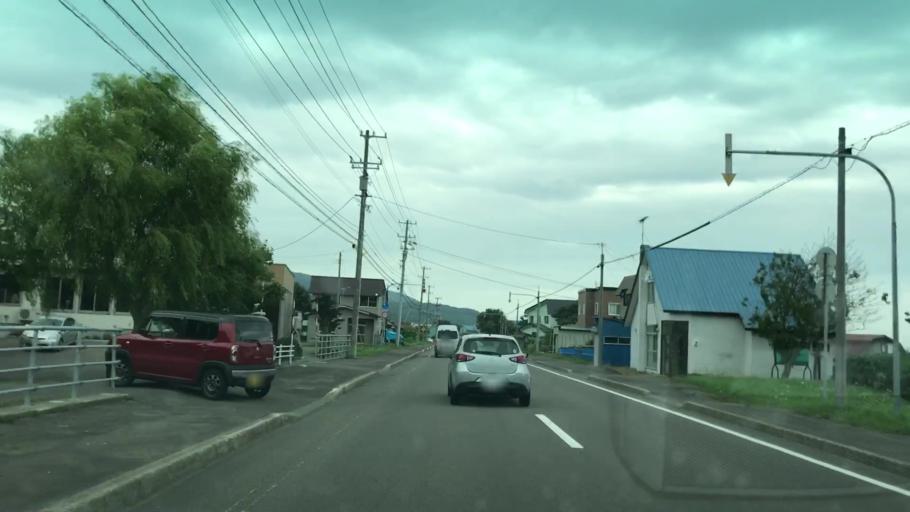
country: JP
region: Hokkaido
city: Iwanai
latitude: 42.7644
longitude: 140.2528
